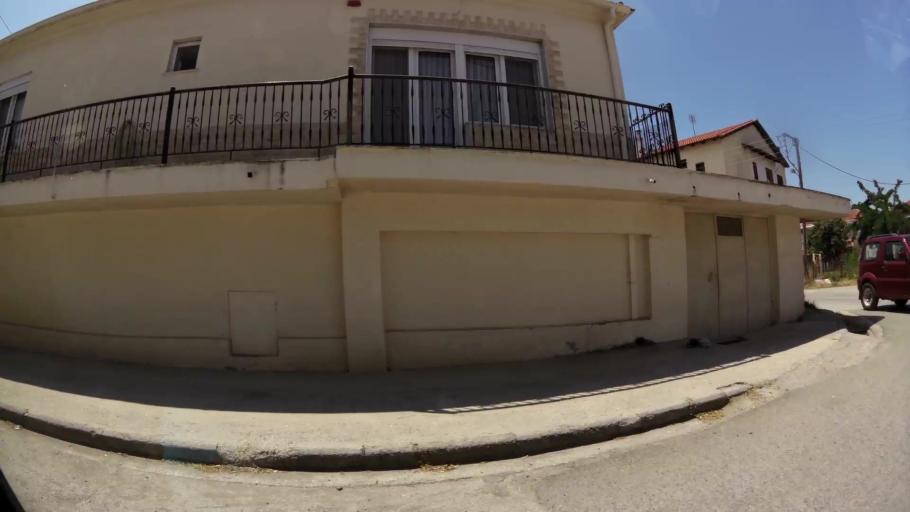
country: GR
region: Central Macedonia
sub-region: Nomos Thessalonikis
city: Epanomi
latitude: 40.4297
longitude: 22.9234
